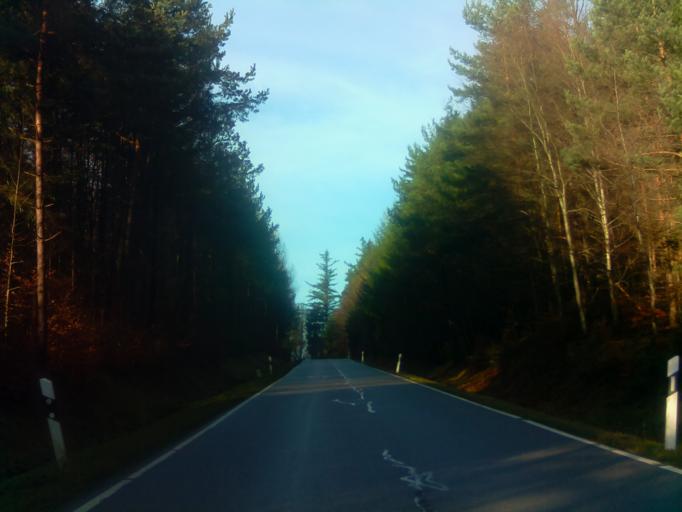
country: DE
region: Hesse
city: Reichelsheim
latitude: 49.6777
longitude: 8.9029
